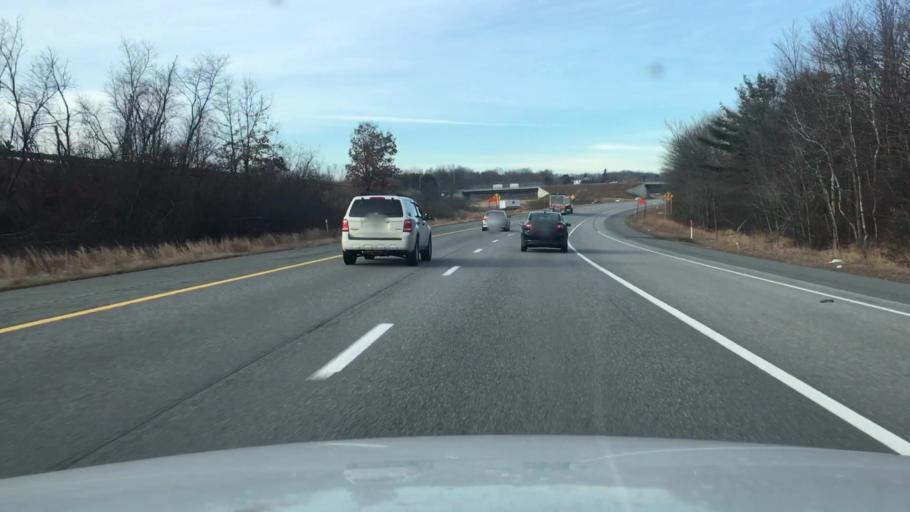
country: US
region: New Hampshire
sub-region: Hillsborough County
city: Manchester
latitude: 42.9651
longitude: -71.4114
